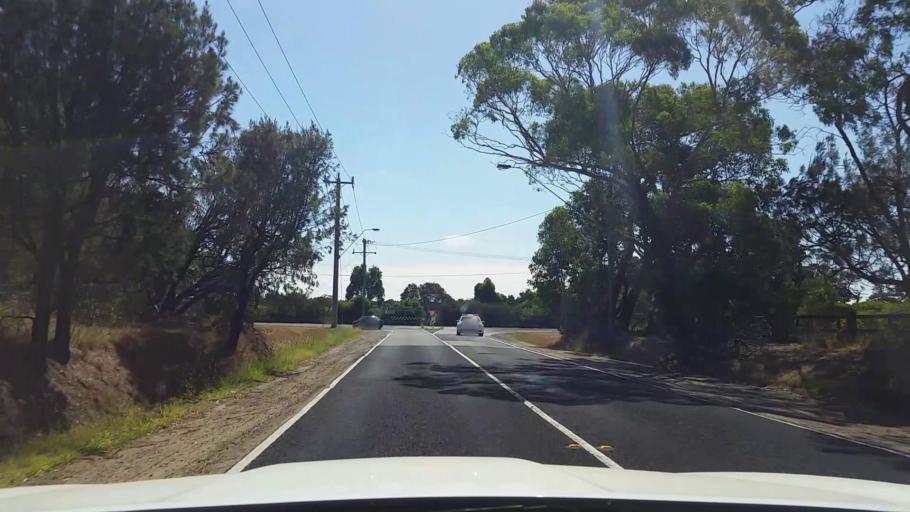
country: AU
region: Victoria
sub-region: Mornington Peninsula
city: Baxter
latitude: -38.2057
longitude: 145.1586
